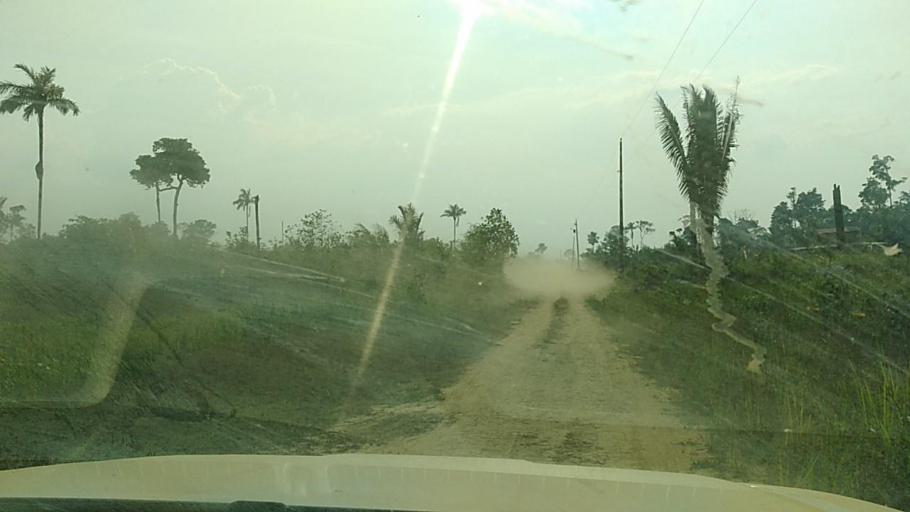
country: BR
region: Rondonia
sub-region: Porto Velho
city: Porto Velho
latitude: -8.5644
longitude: -64.0327
